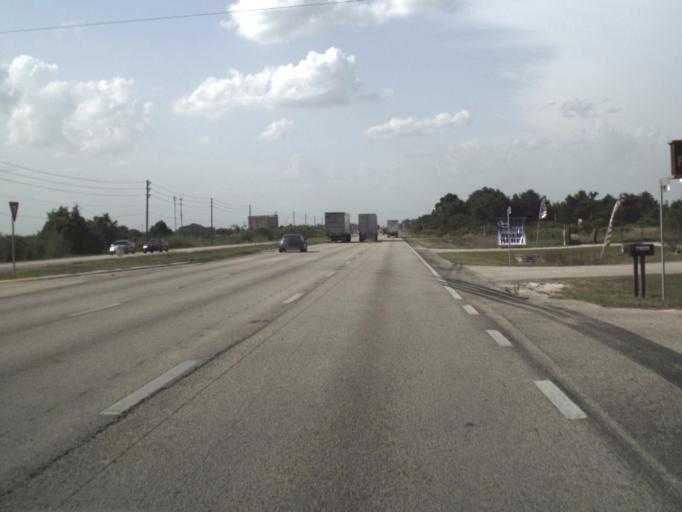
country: US
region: Florida
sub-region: Polk County
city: Lake Wales
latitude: 27.9408
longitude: -81.6132
